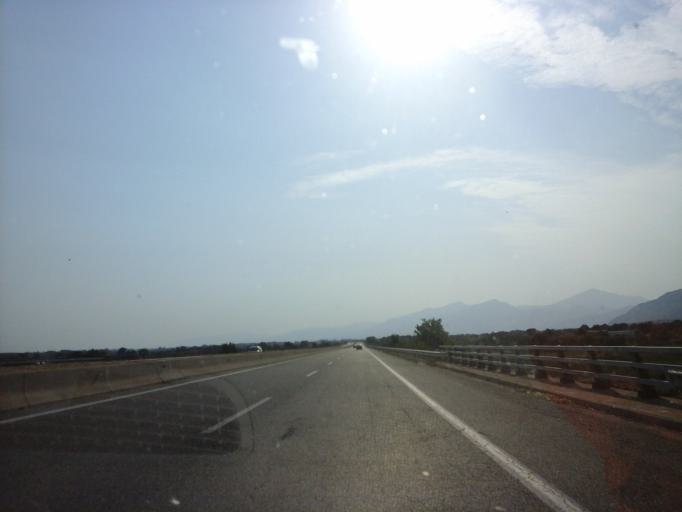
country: GR
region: East Macedonia and Thrace
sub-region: Nomos Xanthis
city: Selero
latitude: 41.1200
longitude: 25.0586
